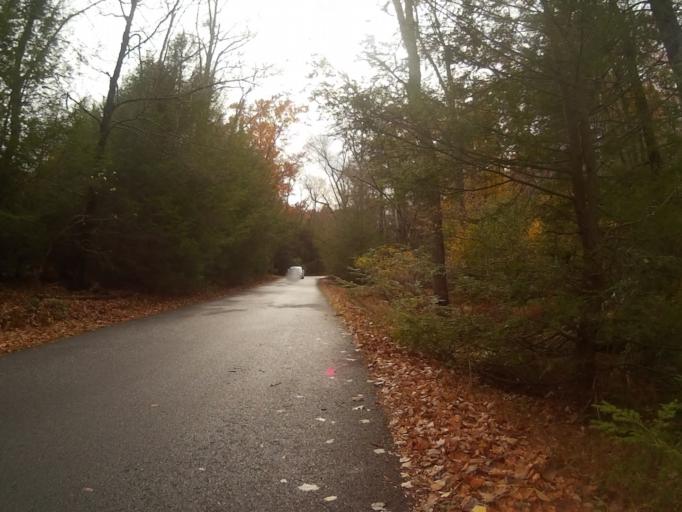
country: US
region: Pennsylvania
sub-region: Centre County
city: Boalsburg
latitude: 40.7553
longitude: -77.7366
